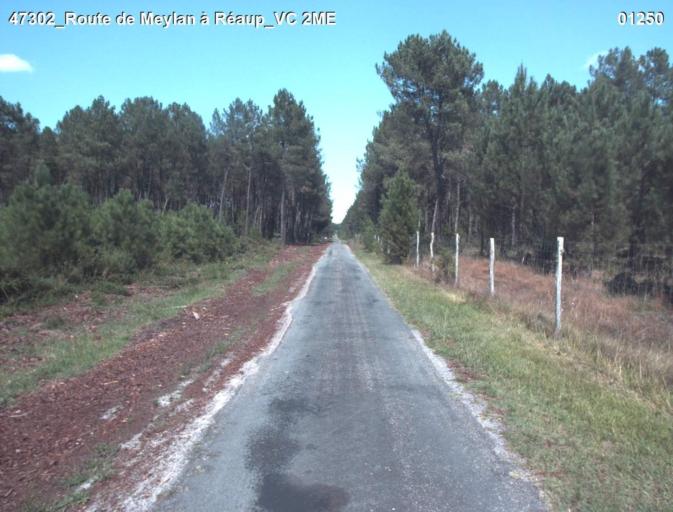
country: FR
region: Aquitaine
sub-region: Departement du Lot-et-Garonne
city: Mezin
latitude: 44.0978
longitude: 0.1336
